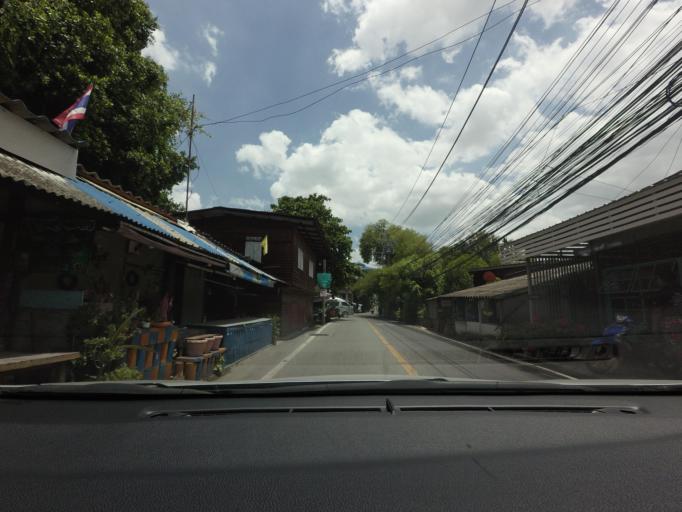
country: TH
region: Samut Prakan
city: Phra Samut Chedi
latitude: 13.6253
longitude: 100.5835
